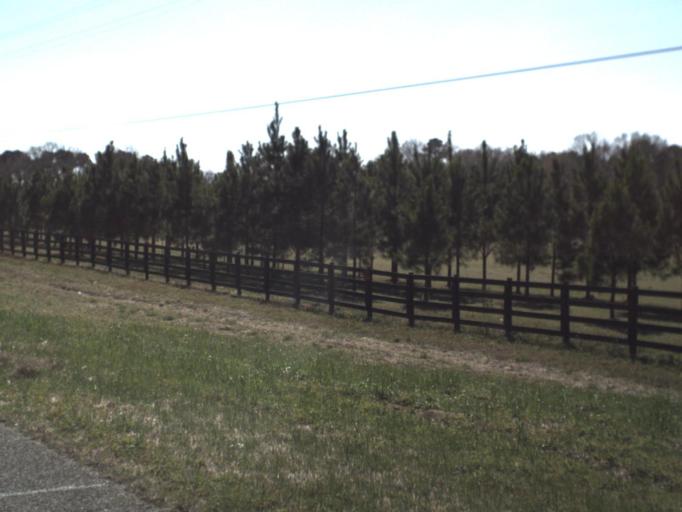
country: US
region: Florida
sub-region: Jackson County
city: Graceville
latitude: 30.9230
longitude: -85.3840
